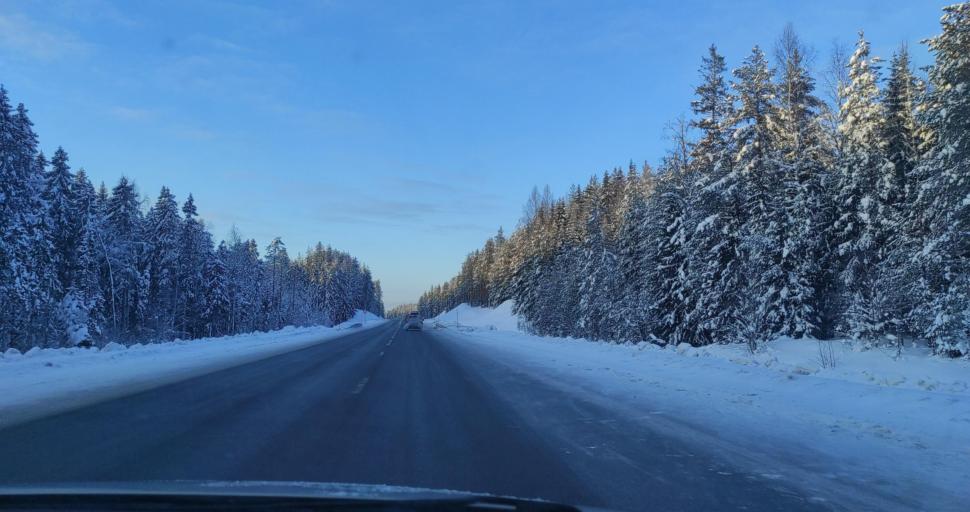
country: RU
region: Republic of Karelia
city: Pryazha
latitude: 61.8018
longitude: 33.9008
